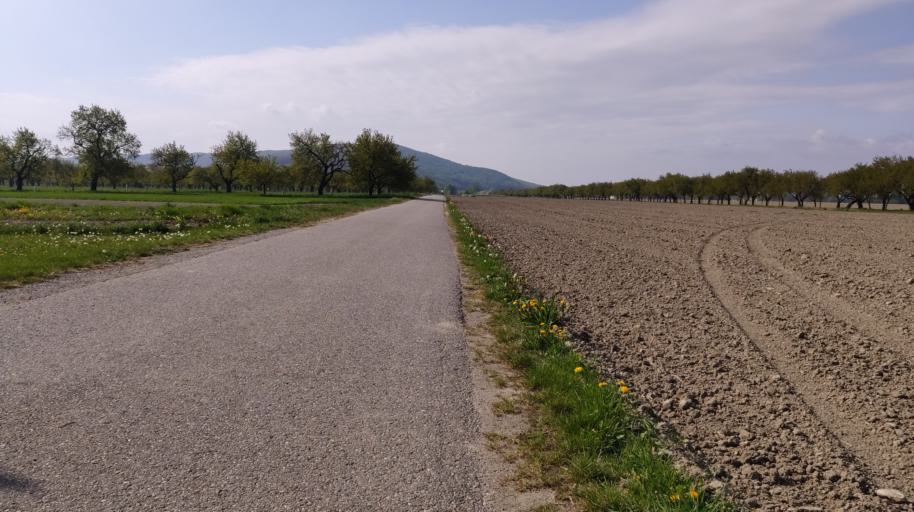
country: AT
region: Burgenland
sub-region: Politischer Bezirk Neusiedl am See
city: Kittsee
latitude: 48.0995
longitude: 17.0580
